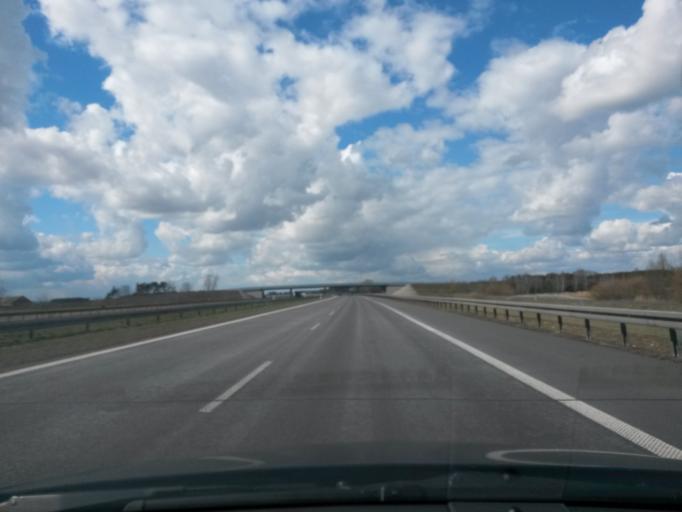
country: PL
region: Greater Poland Voivodeship
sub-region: Powiat kolski
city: Dabie
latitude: 52.0892
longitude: 18.7879
